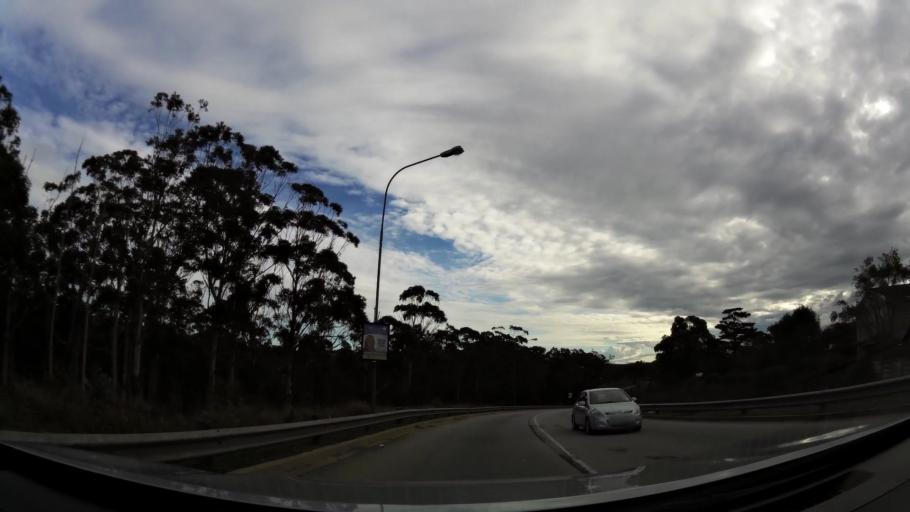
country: ZA
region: Eastern Cape
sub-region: Nelson Mandela Bay Metropolitan Municipality
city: Port Elizabeth
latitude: -33.9531
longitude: 25.5120
